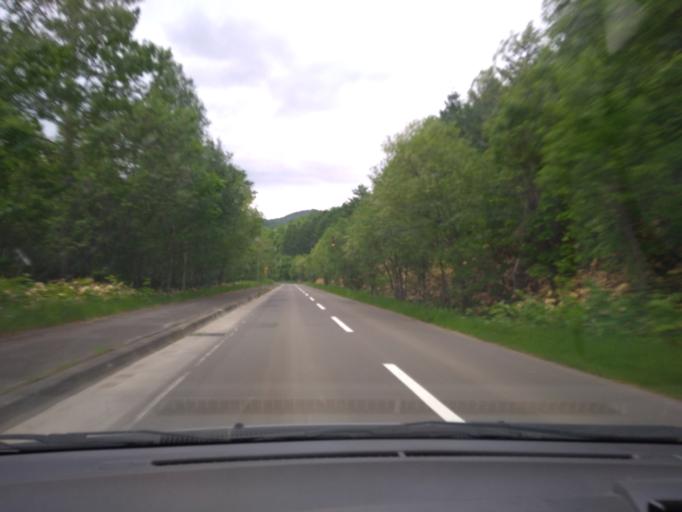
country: JP
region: Hokkaido
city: Shimo-furano
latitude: 43.1567
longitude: 142.5049
